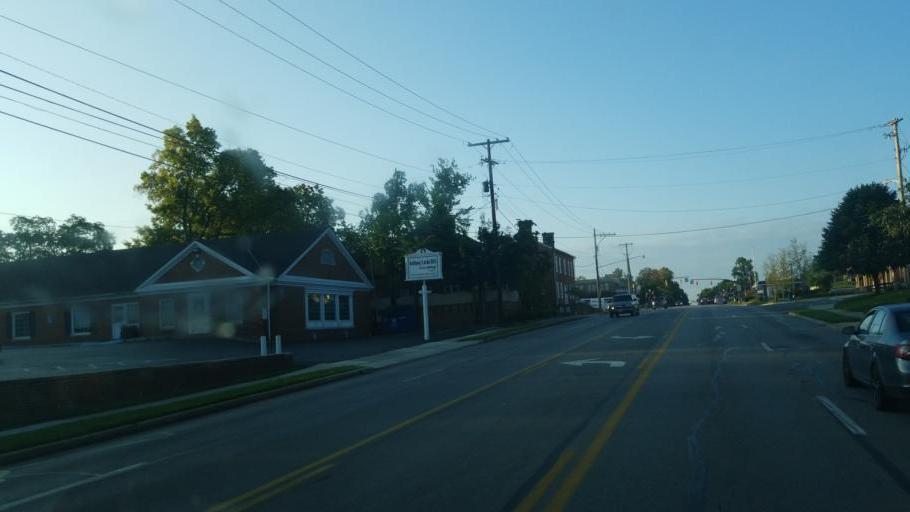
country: US
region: Ohio
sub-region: Franklin County
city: Worthington
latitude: 40.0946
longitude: -83.0178
